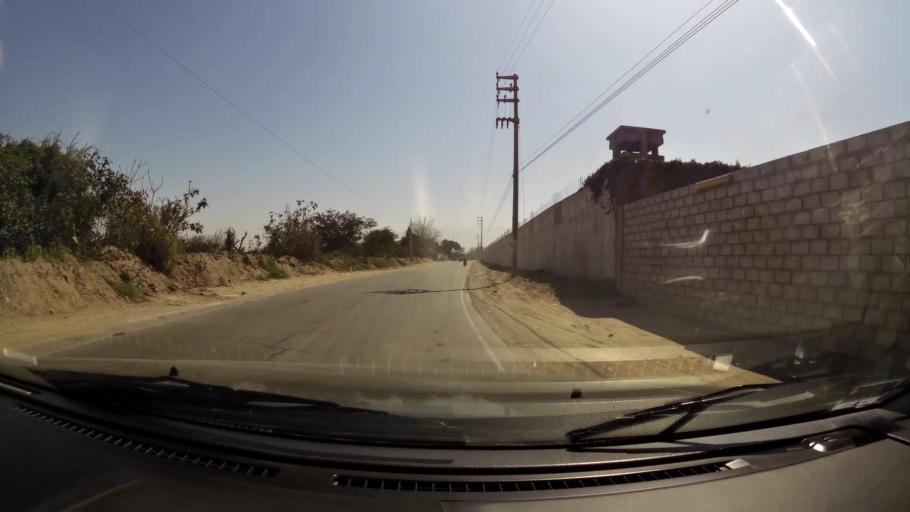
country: PE
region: Ica
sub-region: Provincia de Ica
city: La Tinguina
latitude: -14.0098
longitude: -75.7055
